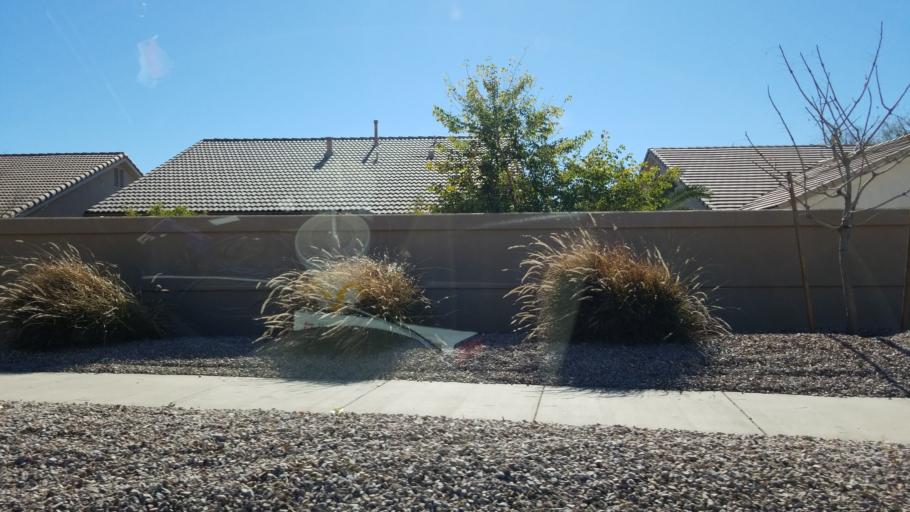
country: US
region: Arizona
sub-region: Maricopa County
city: Chandler
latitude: 33.3207
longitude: -111.8141
